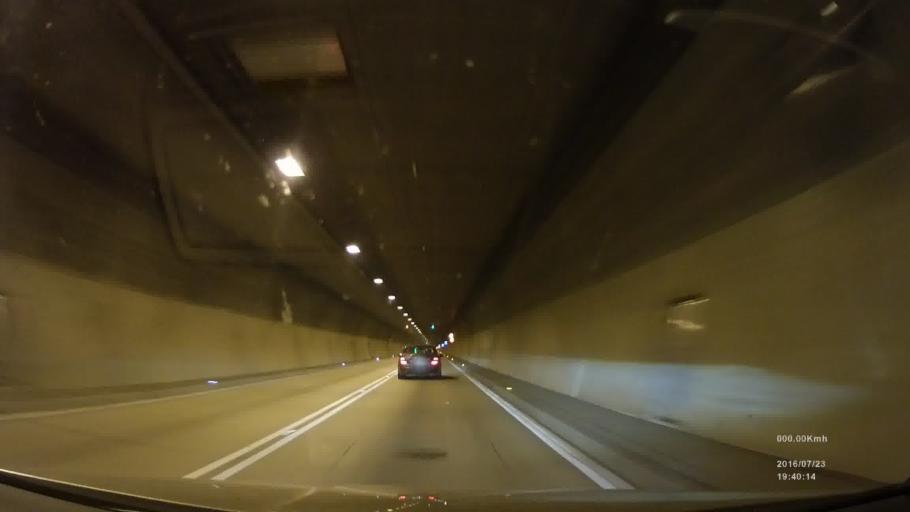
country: SK
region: Kosicky
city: Krompachy
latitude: 49.0034
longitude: 20.8759
